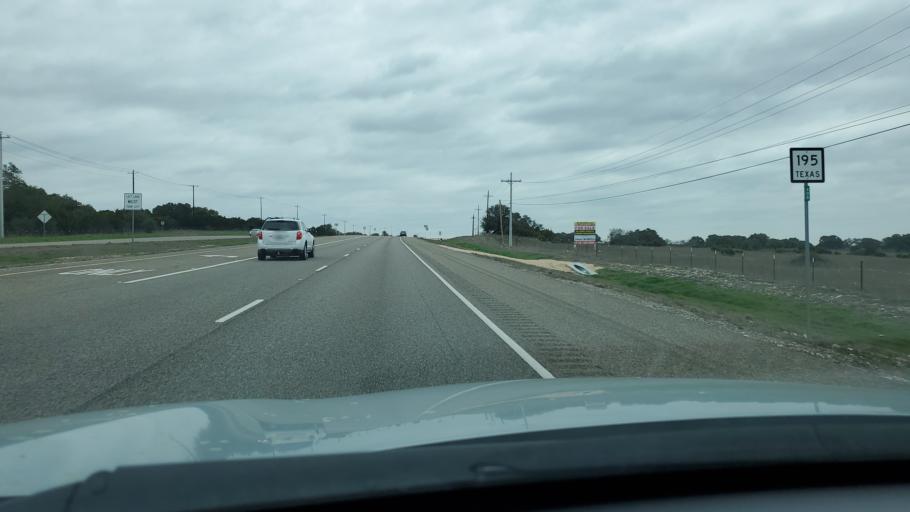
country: US
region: Texas
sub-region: Williamson County
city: Florence
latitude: 30.7914
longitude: -97.7659
